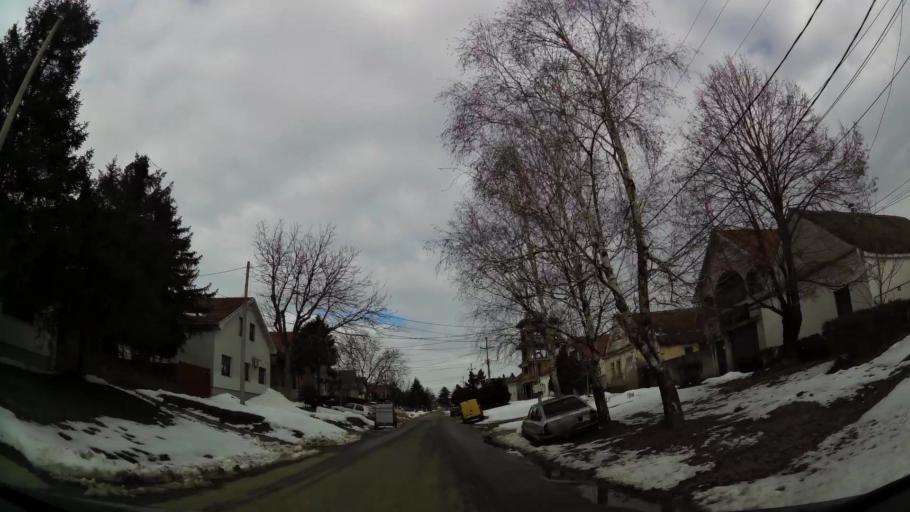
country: RS
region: Central Serbia
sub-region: Belgrade
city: Surcin
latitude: 44.7971
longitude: 20.2846
